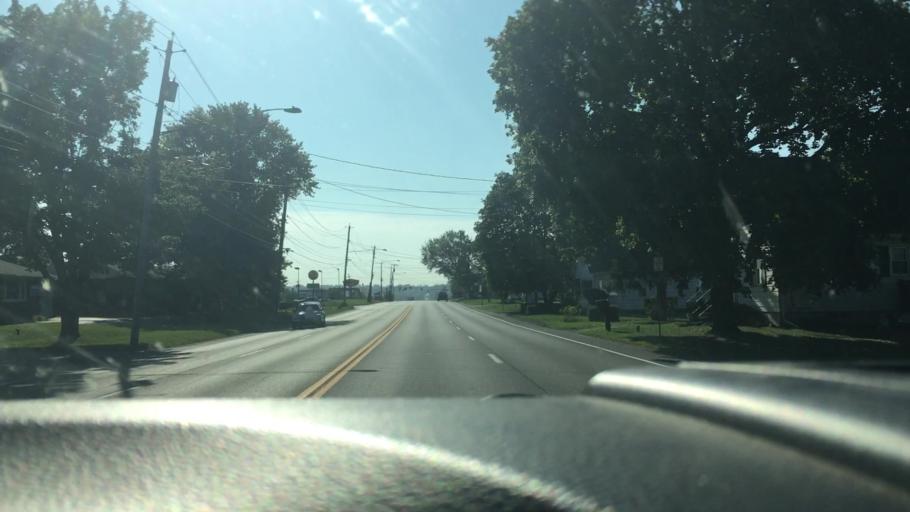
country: US
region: New York
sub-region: Onondaga County
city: Galeville
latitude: 43.0946
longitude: -76.1748
